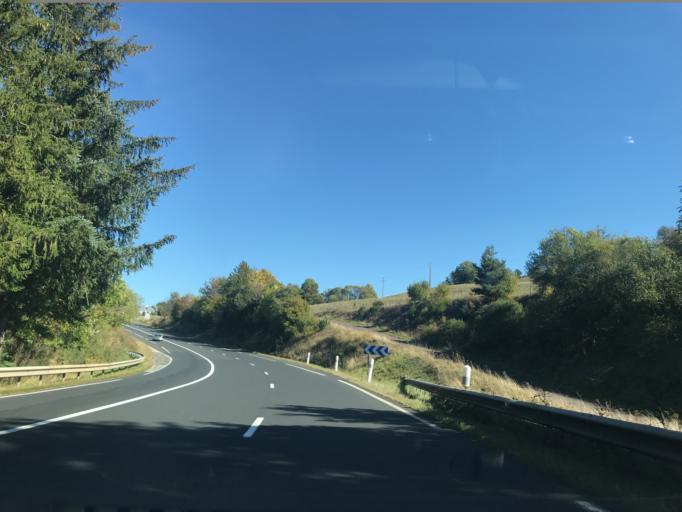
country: FR
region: Auvergne
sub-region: Departement du Puy-de-Dome
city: Gelles
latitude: 45.6758
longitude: 2.7957
